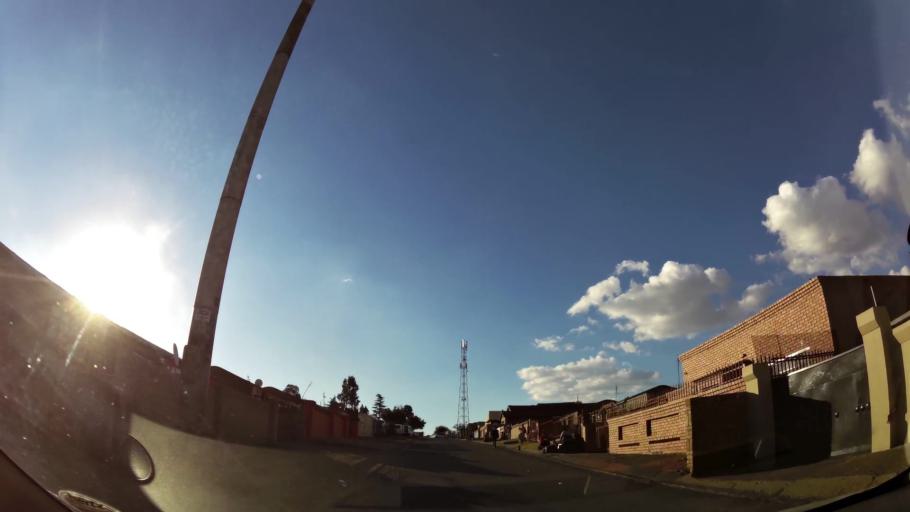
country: ZA
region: Mpumalanga
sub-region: Nkangala District Municipality
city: Witbank
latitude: -25.8763
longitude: 29.1797
